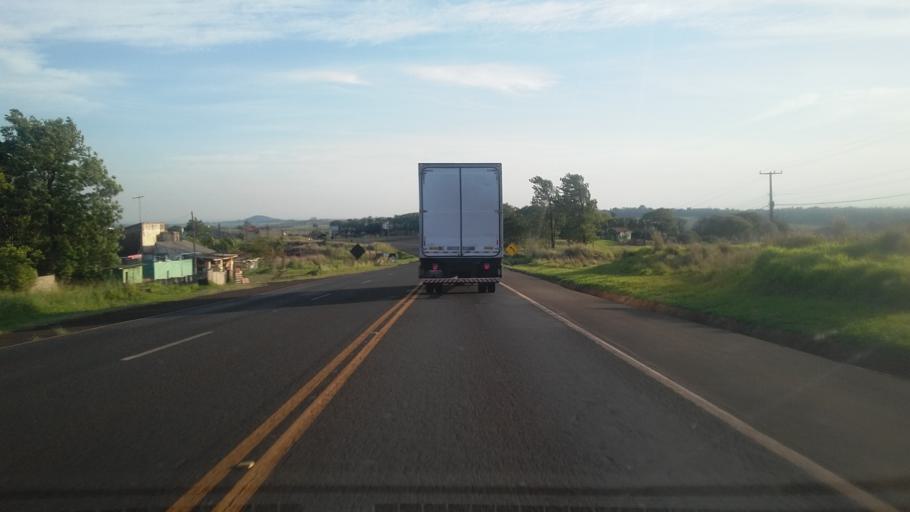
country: BR
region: Parana
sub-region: Bandeirantes
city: Bandeirantes
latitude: -23.1686
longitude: -50.6122
